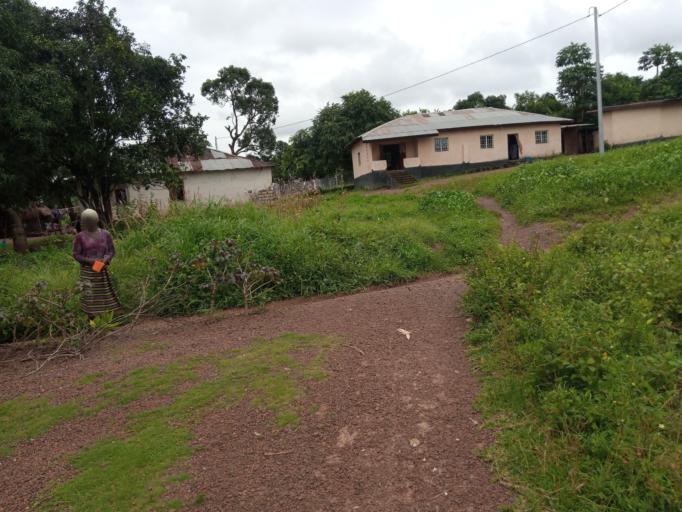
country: SL
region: Southern Province
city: Largo
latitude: 8.1998
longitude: -12.0603
